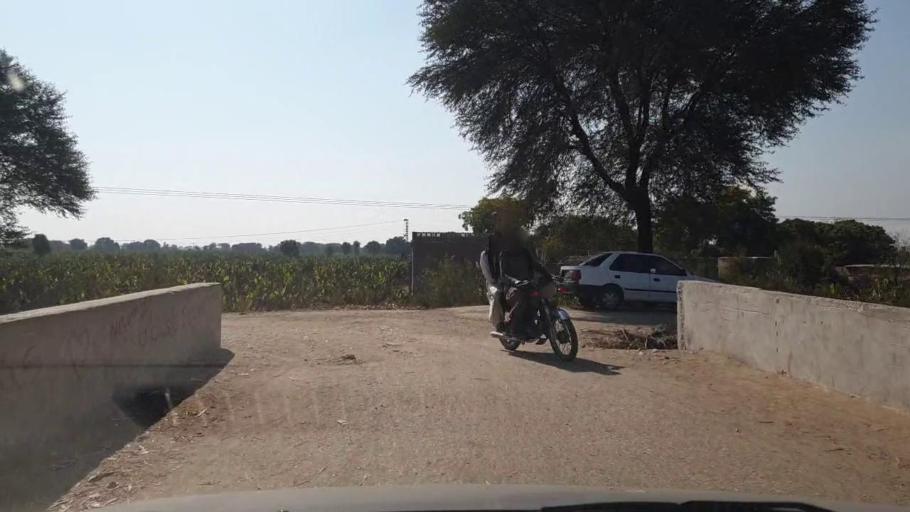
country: PK
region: Sindh
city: Tando Jam
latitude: 25.4498
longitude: 68.6239
